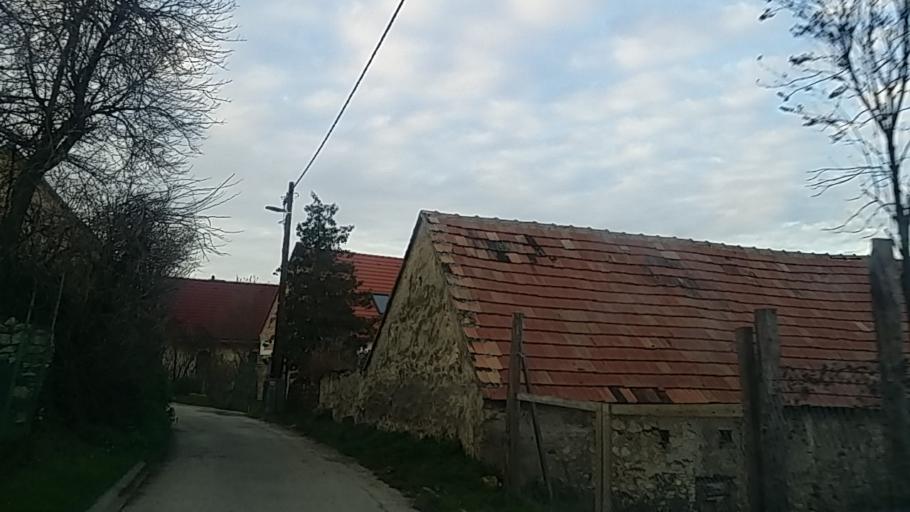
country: HU
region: Veszprem
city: Urkut
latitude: 46.9851
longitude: 17.6940
